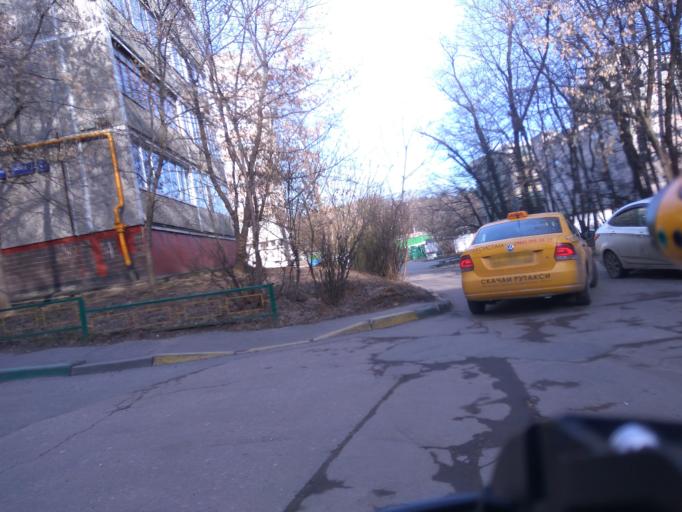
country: RU
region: Moscow
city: Davydkovo
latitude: 55.7246
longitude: 37.4777
